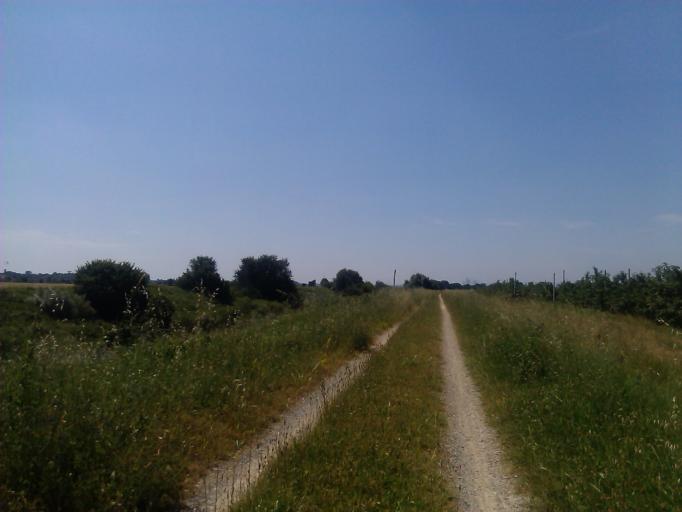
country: IT
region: Tuscany
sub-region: Province of Arezzo
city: Tegoleto
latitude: 43.3697
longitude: 11.8256
